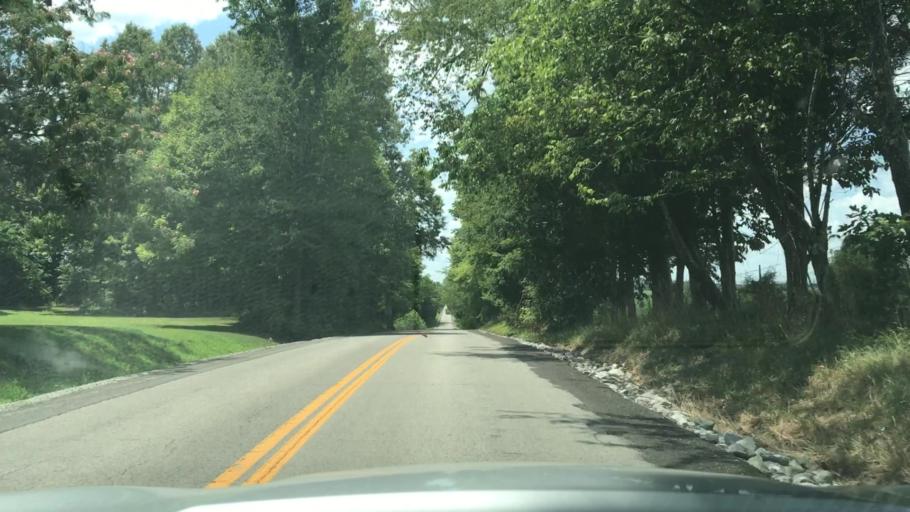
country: US
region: Kentucky
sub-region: Muhlenberg County
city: Greenville
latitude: 37.1333
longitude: -87.2785
